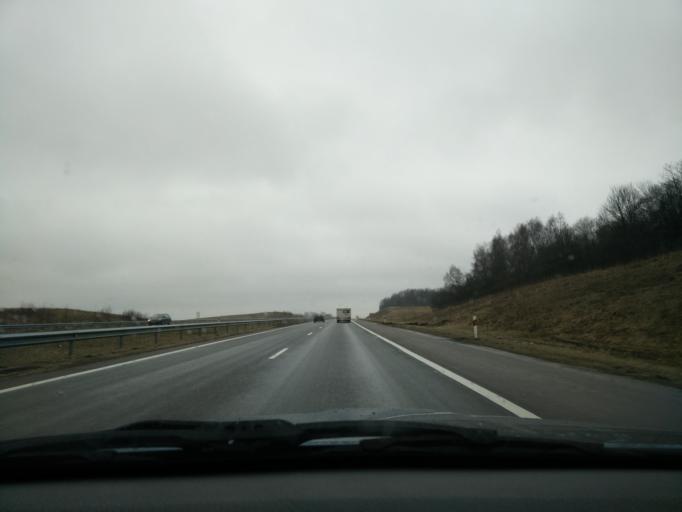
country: LT
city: Skaudvile
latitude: 55.5075
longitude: 22.4116
